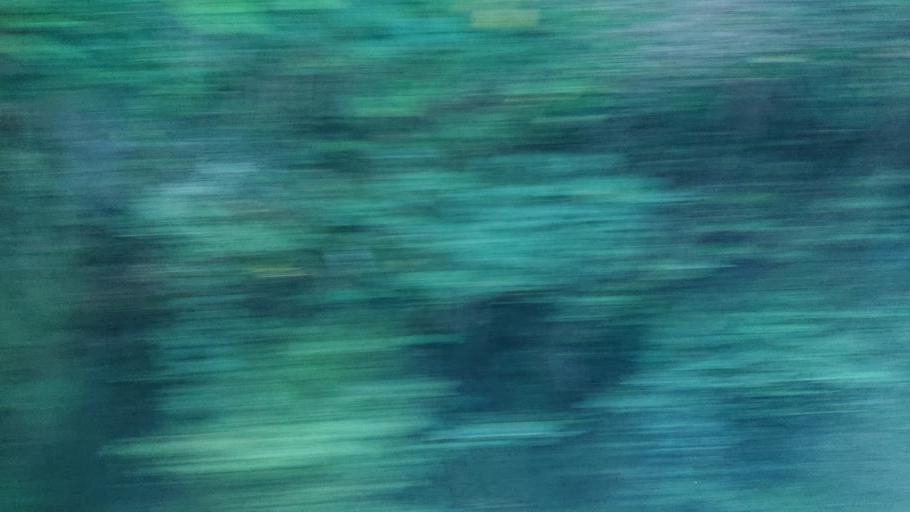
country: TW
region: Taiwan
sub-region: Yunlin
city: Douliu
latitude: 23.5315
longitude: 120.6547
